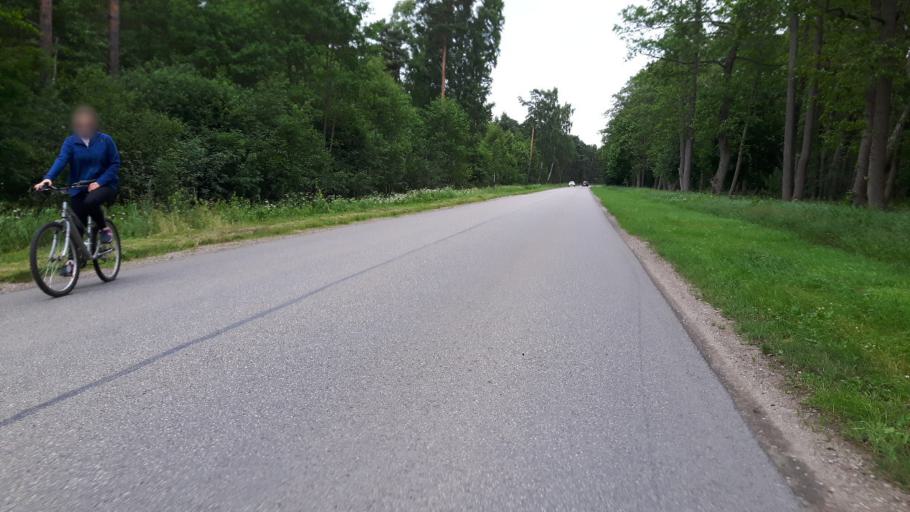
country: LV
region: Liepaja
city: Vec-Liepaja
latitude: 56.5650
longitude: 21.0152
